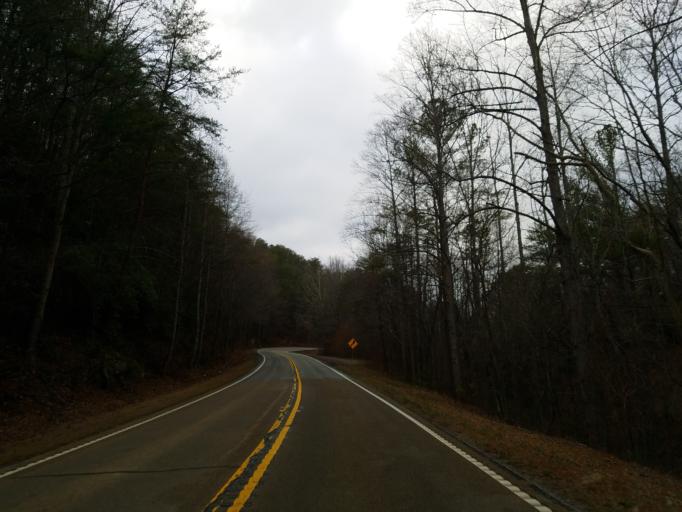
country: US
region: Georgia
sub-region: Bartow County
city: Rydal
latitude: 34.3455
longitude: -84.6440
